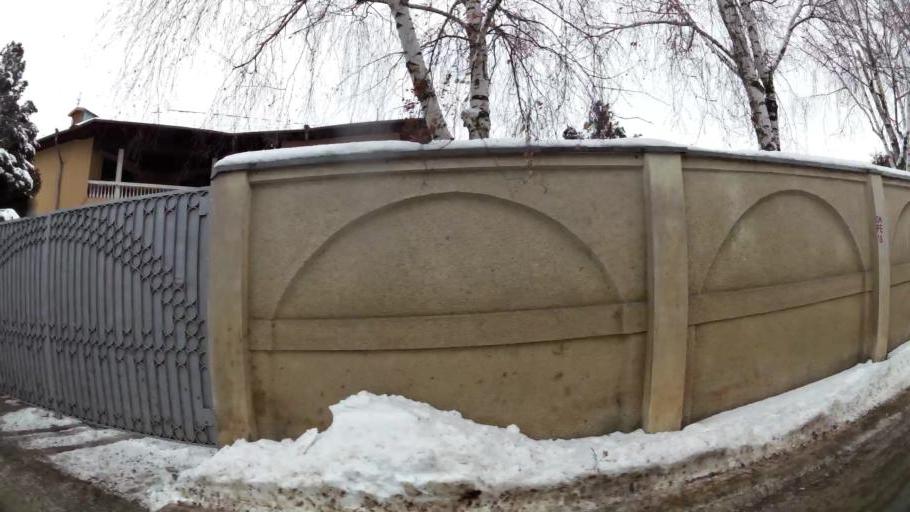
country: RO
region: Ilfov
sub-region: Comuna Otopeni
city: Otopeni
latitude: 44.5137
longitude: 26.1038
